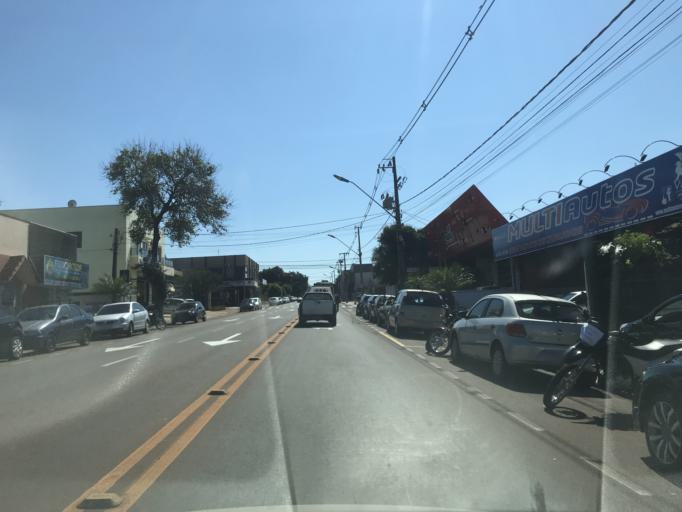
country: BR
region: Parana
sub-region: Toledo
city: Toledo
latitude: -24.7318
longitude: -53.7361
